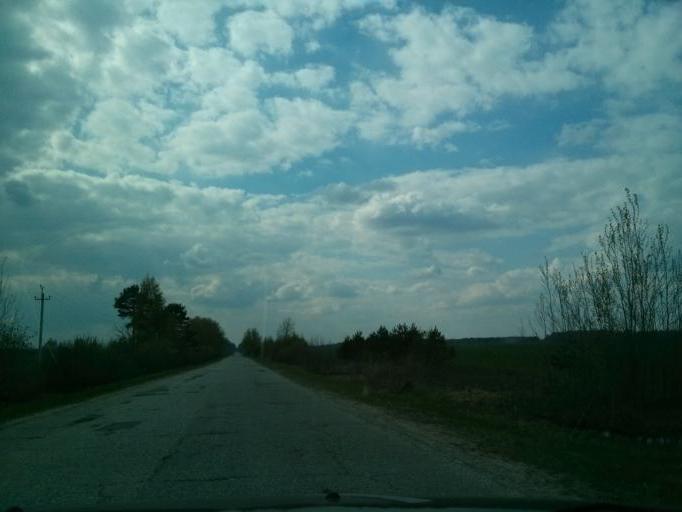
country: RU
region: Nizjnij Novgorod
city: Shimorskoye
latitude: 55.3369
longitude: 41.9002
